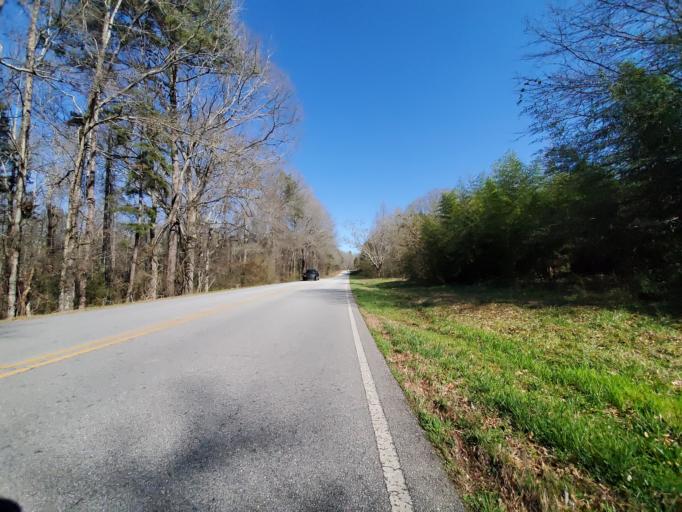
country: US
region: Georgia
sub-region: Oconee County
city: Bogart
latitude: 34.0000
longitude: -83.4955
